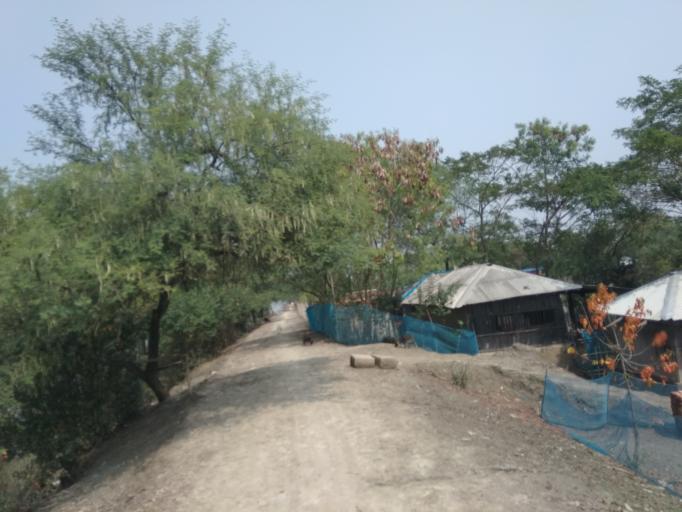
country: IN
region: West Bengal
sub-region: North 24 Parganas
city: Gosaba
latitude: 22.2475
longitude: 89.2498
